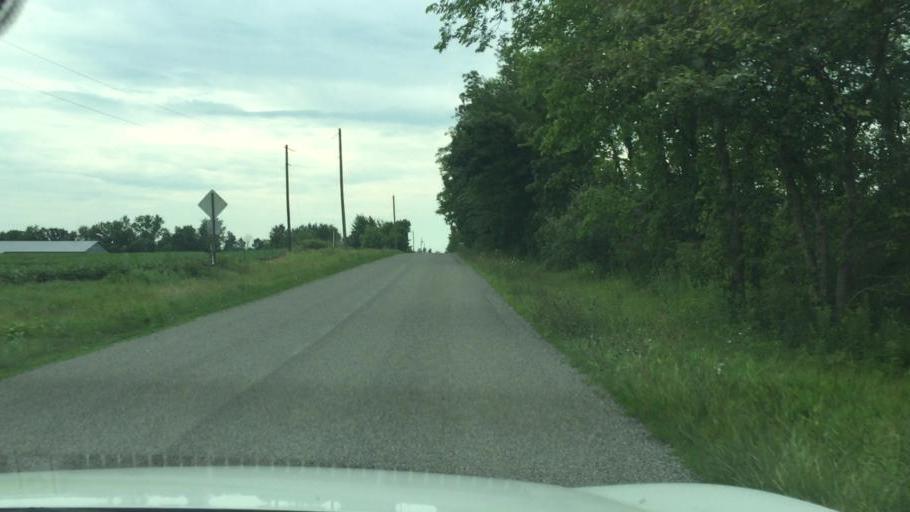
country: US
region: Ohio
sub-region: Champaign County
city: North Lewisburg
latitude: 40.2642
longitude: -83.5027
